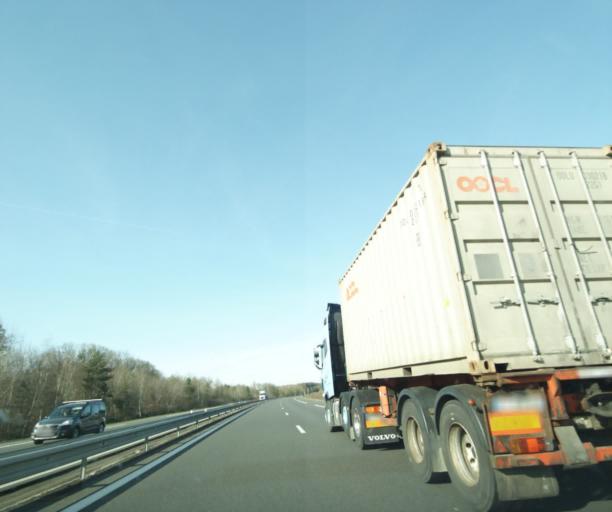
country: FR
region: Centre
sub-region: Departement du Loiret
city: Jouy-le-Potier
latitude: 47.7847
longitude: 1.8464
